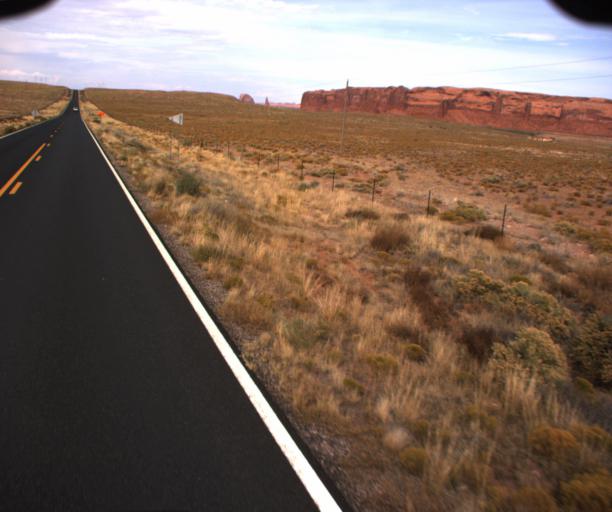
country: US
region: Arizona
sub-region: Apache County
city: Many Farms
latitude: 36.5905
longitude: -109.5620
